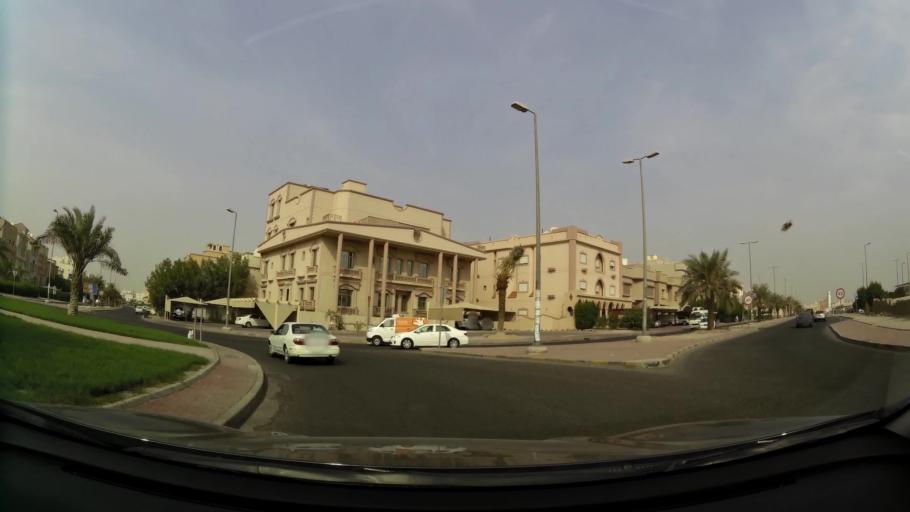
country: KW
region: Al Asimah
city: Ar Rabiyah
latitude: 29.2743
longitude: 47.9343
